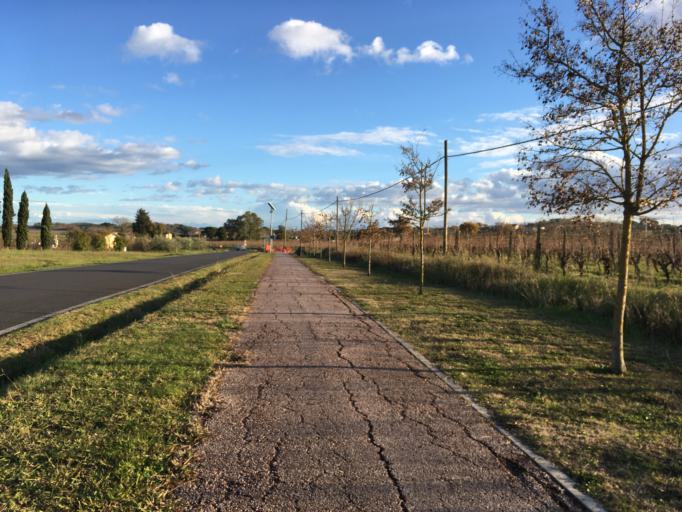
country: IT
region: Tuscany
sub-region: Province of Pisa
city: Cenaia
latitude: 43.6001
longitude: 10.5455
